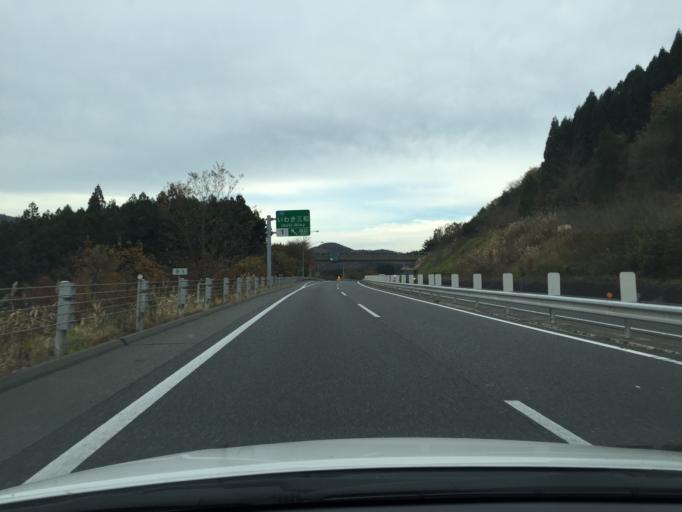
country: JP
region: Fukushima
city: Iwaki
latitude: 37.1047
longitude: 140.7671
